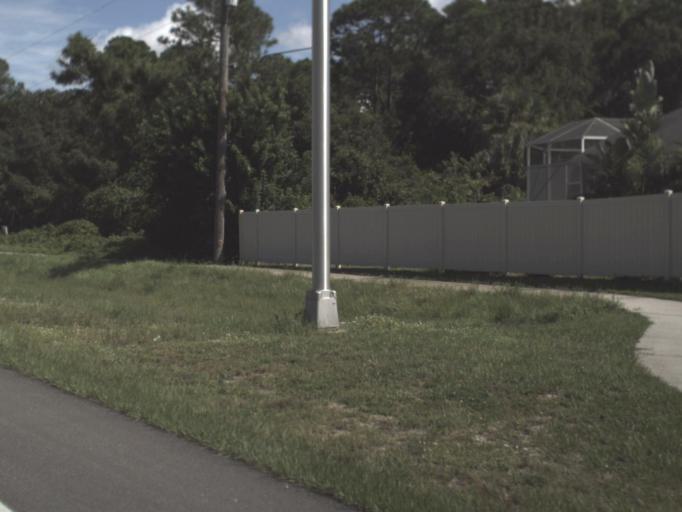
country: US
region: Florida
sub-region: Sarasota County
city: North Port
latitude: 27.0238
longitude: -82.1637
